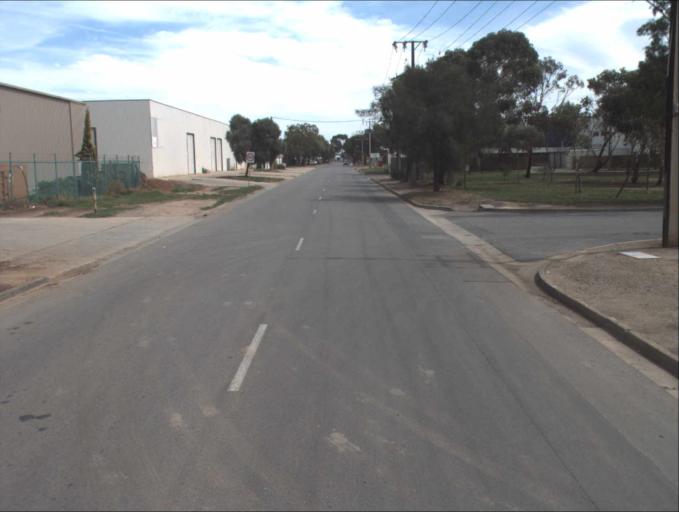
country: AU
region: South Australia
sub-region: Charles Sturt
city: Woodville North
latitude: -34.8391
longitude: 138.5574
